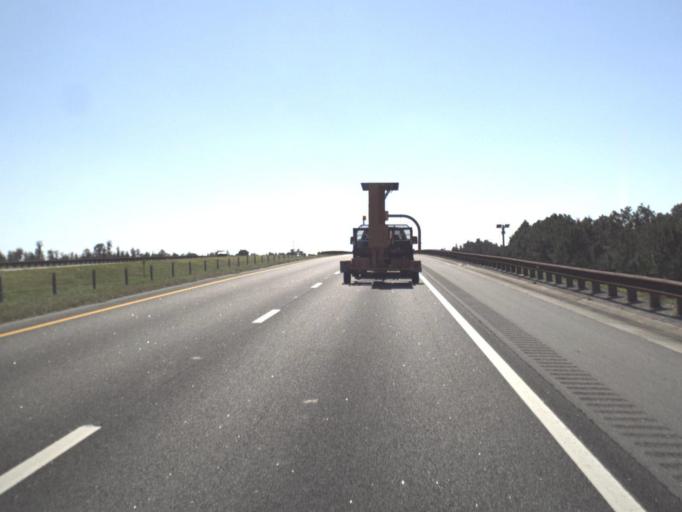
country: US
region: Florida
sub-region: Pasco County
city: Odessa
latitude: 28.2851
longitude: -82.5506
